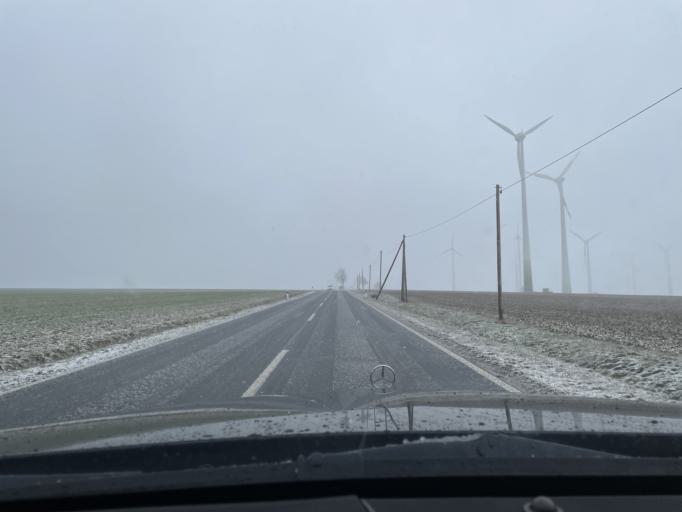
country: DE
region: Thuringia
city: Buttstedt
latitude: 51.2320
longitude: 10.2961
